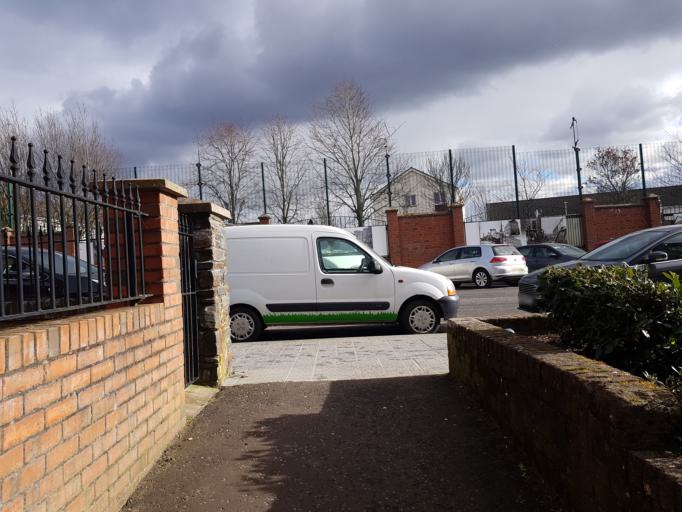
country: GB
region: Northern Ireland
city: Londonderry County Borough
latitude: 54.9933
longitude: -7.3254
